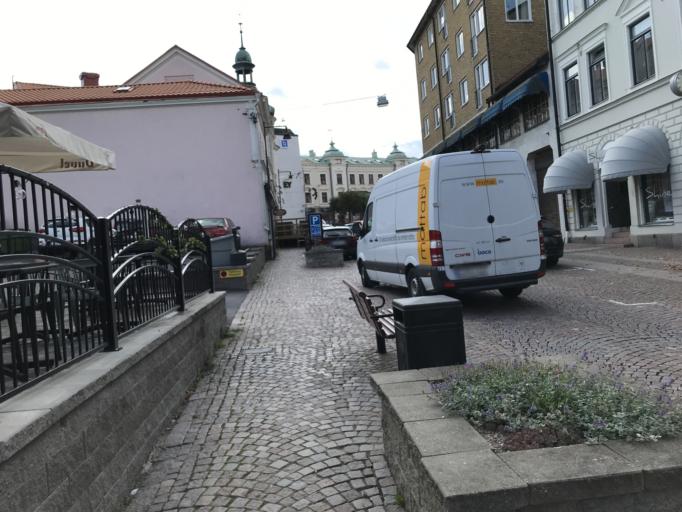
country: SE
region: Kalmar
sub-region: Oskarshamns Kommun
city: Oskarshamn
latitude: 57.2666
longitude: 16.4481
